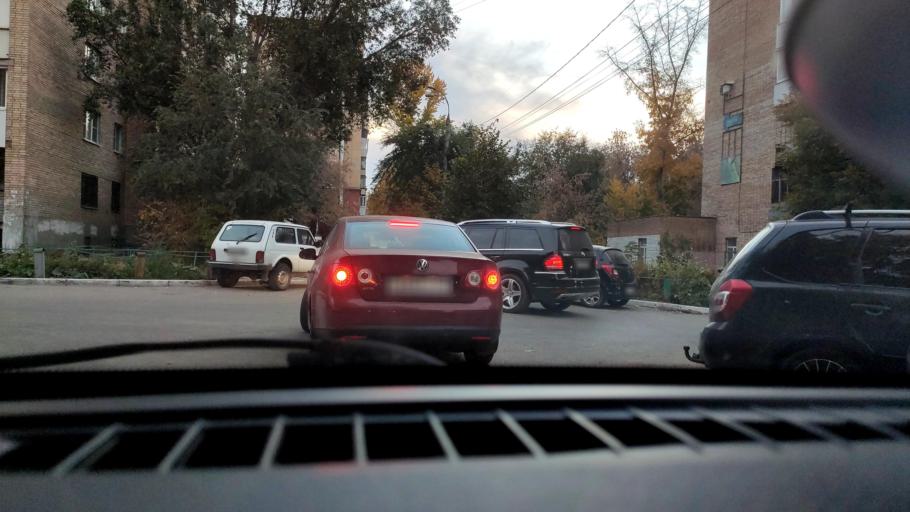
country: RU
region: Samara
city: Samara
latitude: 53.2125
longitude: 50.1386
